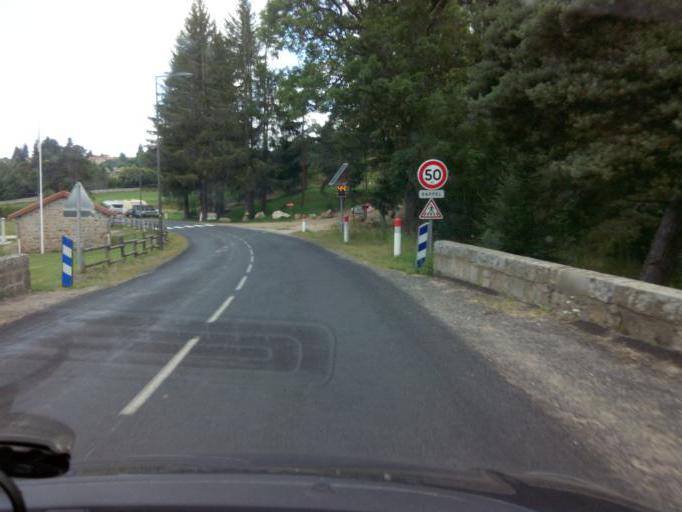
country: FR
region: Rhone-Alpes
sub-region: Departement de la Loire
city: Usson-en-Forez
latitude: 45.3927
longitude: 3.9550
